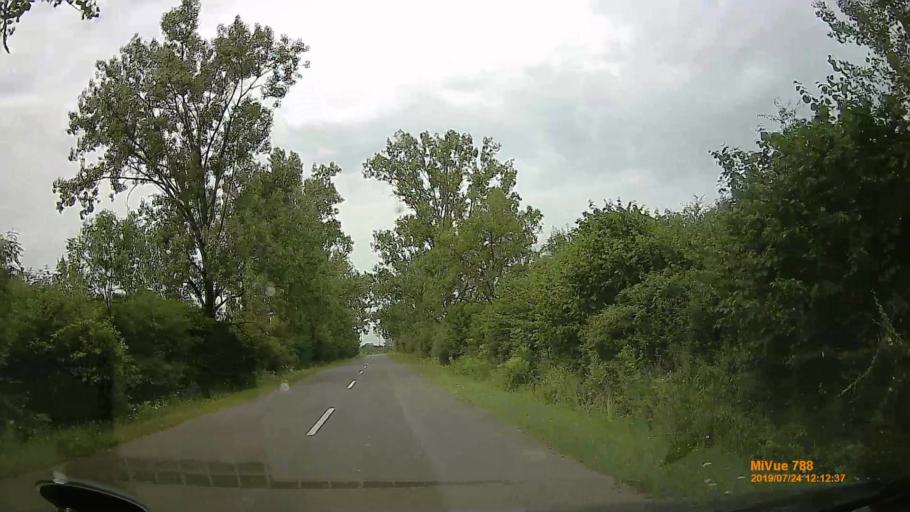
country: HU
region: Szabolcs-Szatmar-Bereg
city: Vasarosnameny
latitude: 48.1966
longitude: 22.3791
